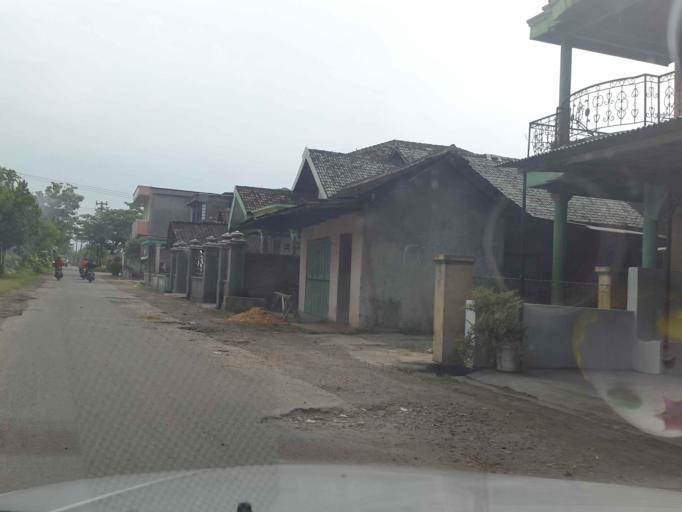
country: ID
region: Central Java
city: Jaten
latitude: -7.5545
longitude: 110.8995
